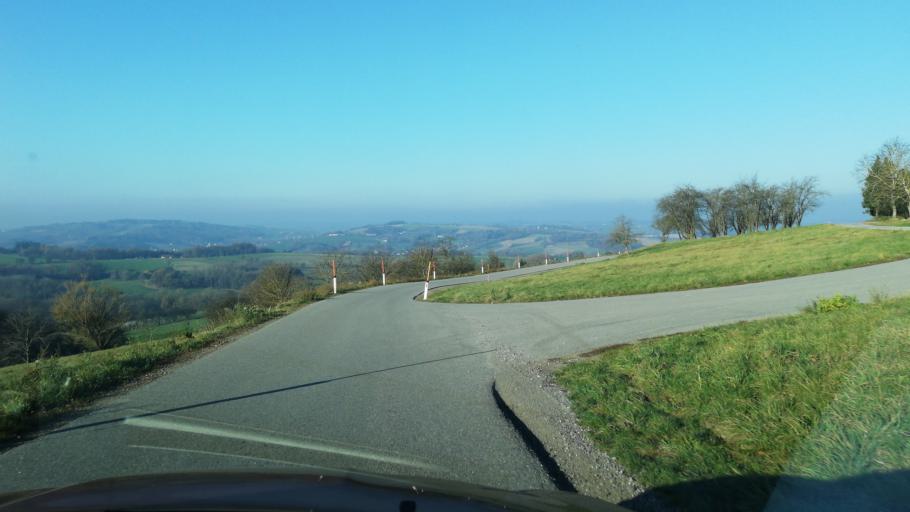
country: AT
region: Upper Austria
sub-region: Wels-Land
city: Buchkirchen
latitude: 48.2547
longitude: 14.0145
